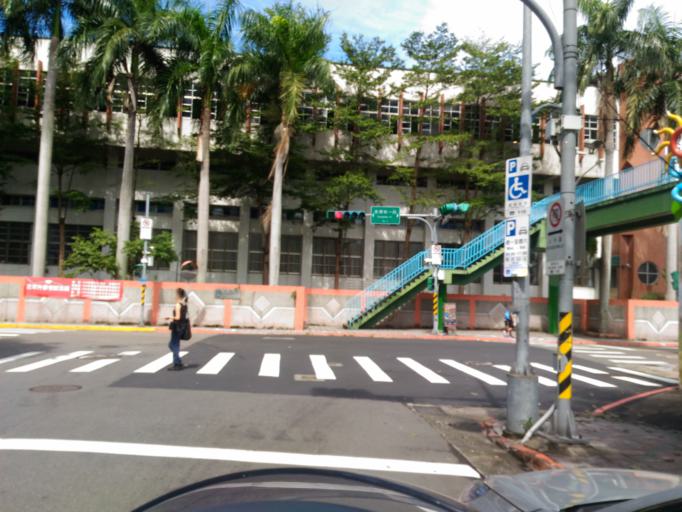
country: TW
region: Taipei
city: Taipei
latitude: 24.9832
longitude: 121.5565
